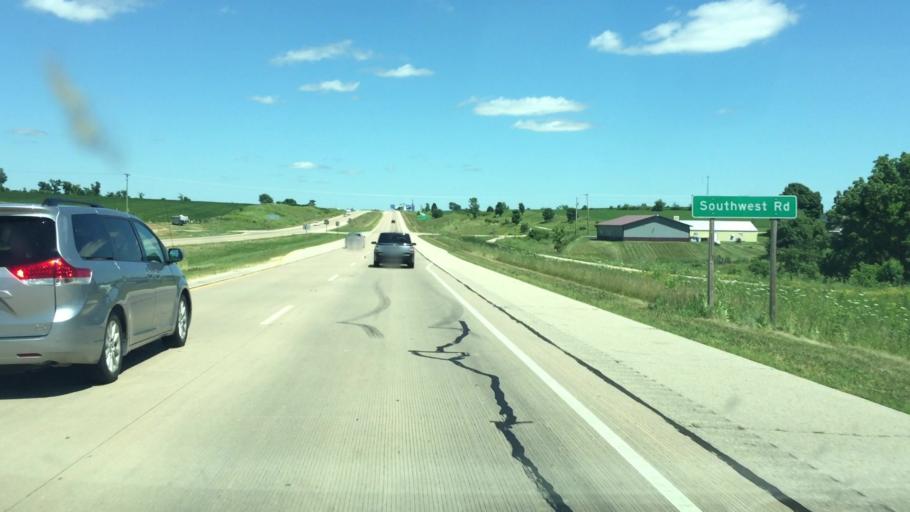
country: US
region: Wisconsin
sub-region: Grant County
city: Platteville
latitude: 42.7109
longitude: -90.5079
